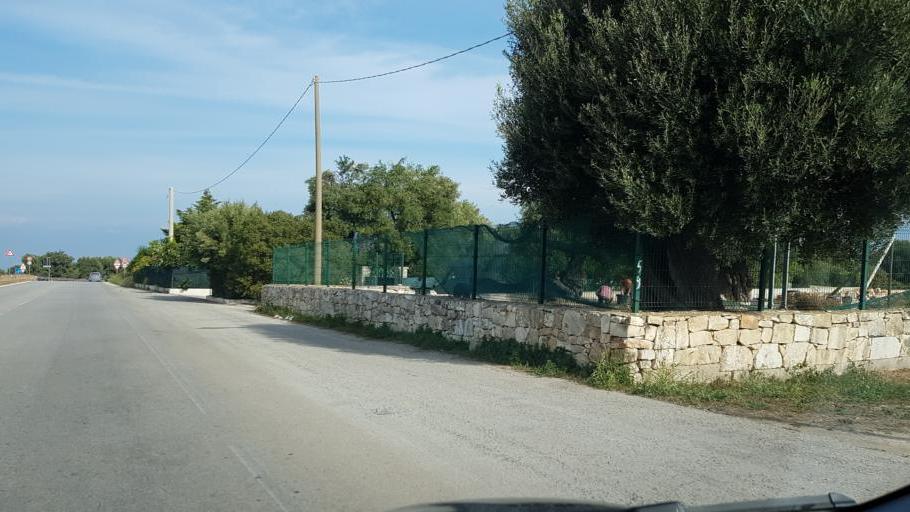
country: IT
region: Apulia
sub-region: Provincia di Brindisi
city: Ostuni
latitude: 40.7549
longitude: 17.5831
